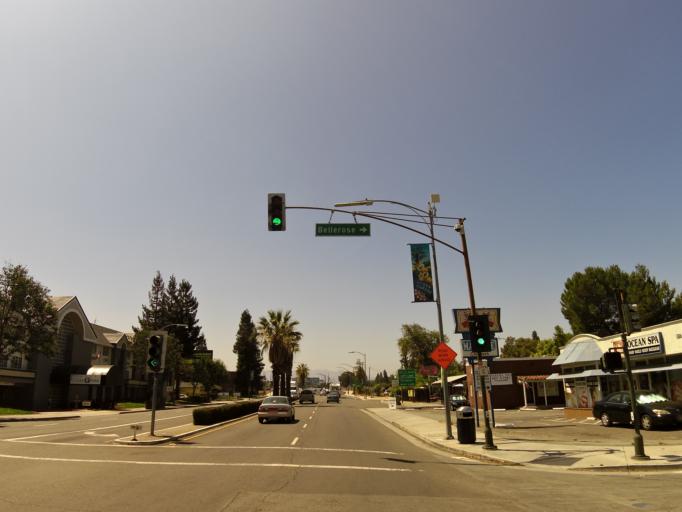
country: US
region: California
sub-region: Santa Clara County
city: Burbank
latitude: 37.3234
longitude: -121.9359
